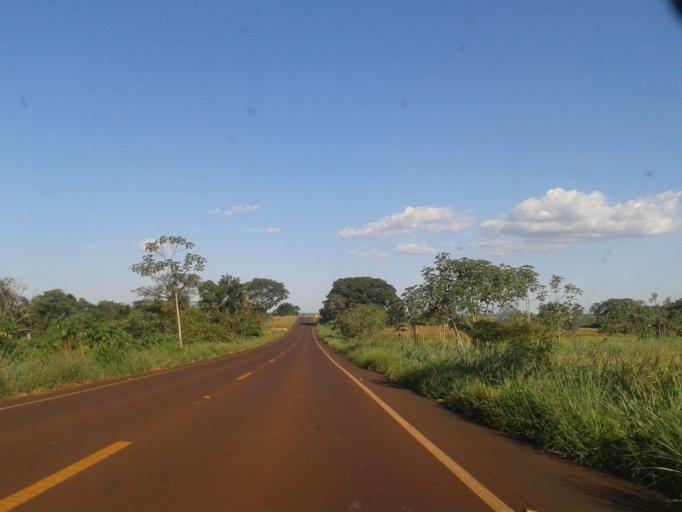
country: BR
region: Minas Gerais
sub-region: Santa Vitoria
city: Santa Vitoria
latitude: -18.7005
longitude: -49.8727
